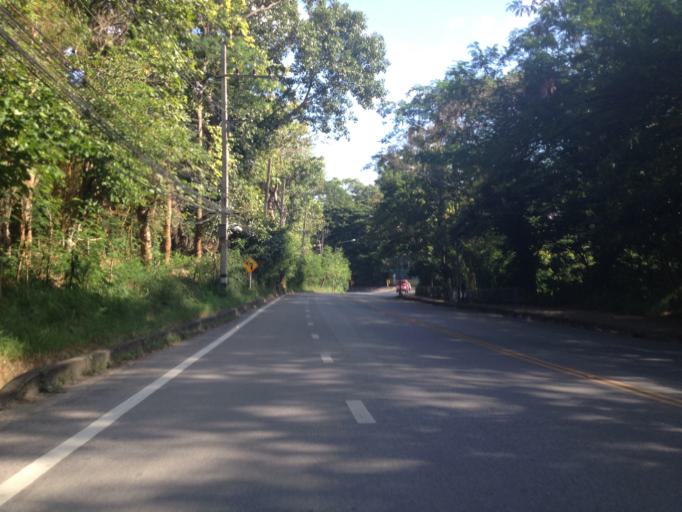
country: TH
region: Chiang Mai
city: Chiang Mai
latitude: 18.8119
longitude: 98.9470
